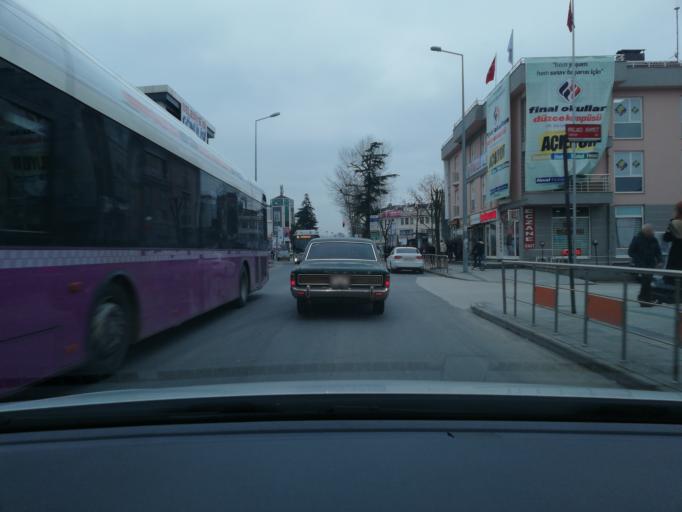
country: TR
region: Duzce
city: Duzce
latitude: 40.8403
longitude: 31.1495
